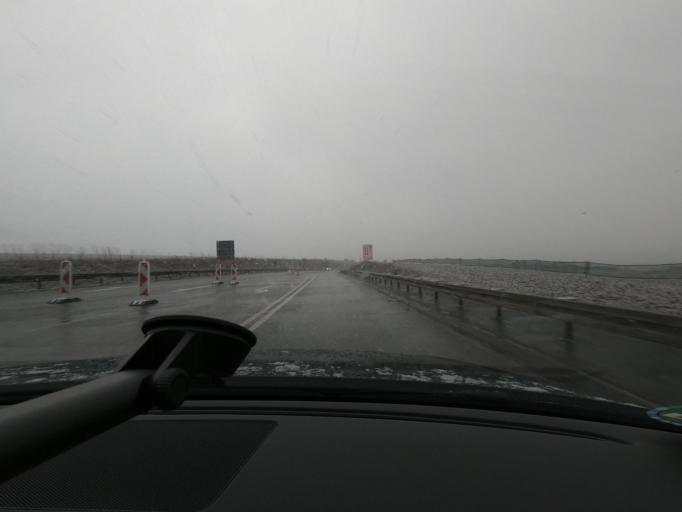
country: DE
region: Thuringia
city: Dingelstadt
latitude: 51.3287
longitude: 10.3264
